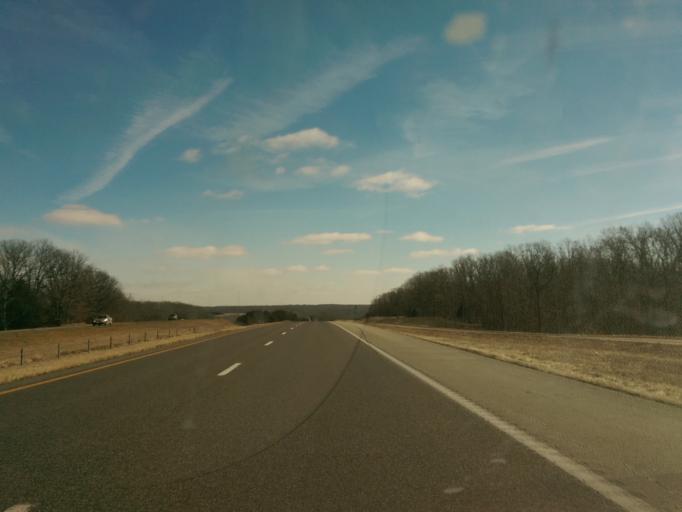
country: US
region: Missouri
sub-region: Callaway County
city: Fulton
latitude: 38.9377
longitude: -91.8593
